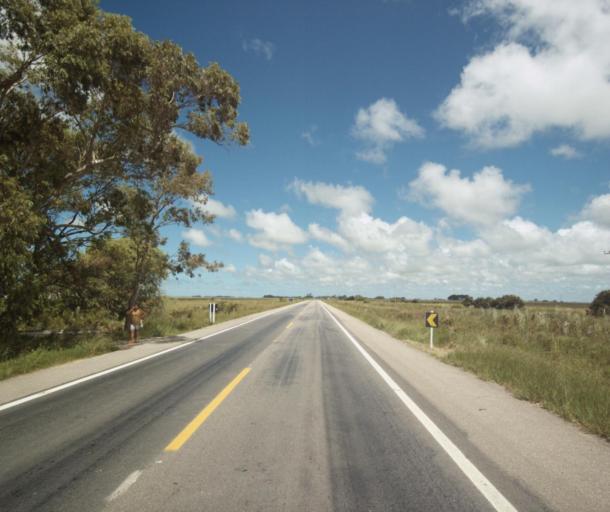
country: UY
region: Cerro Largo
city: Rio Branco
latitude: -32.8580
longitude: -52.7063
